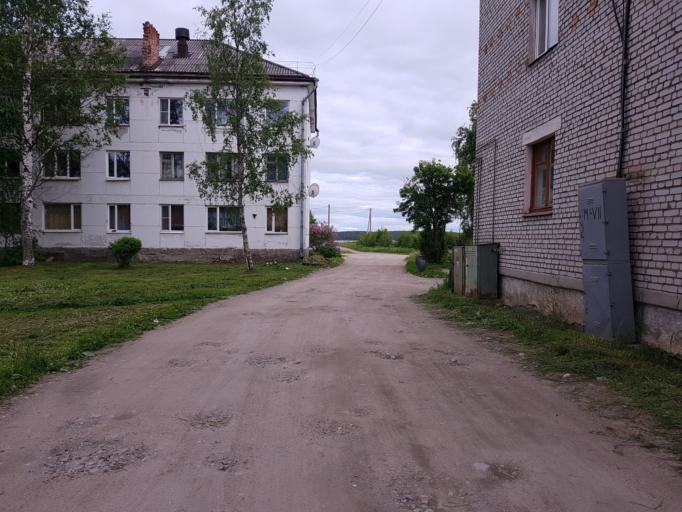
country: RU
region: Republic of Karelia
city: Kalevala
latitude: 65.1963
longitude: 31.1990
